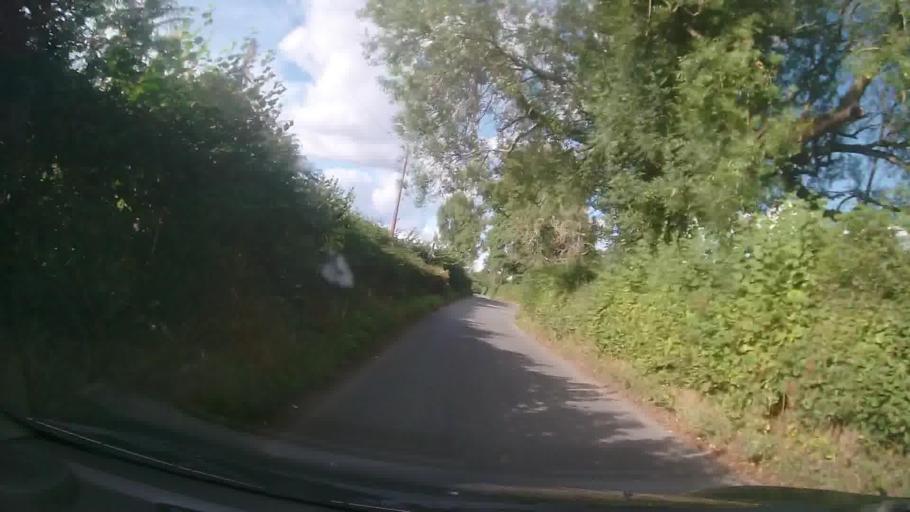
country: GB
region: Wales
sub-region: Sir Powys
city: Brecon
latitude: 51.8851
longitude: -3.3020
